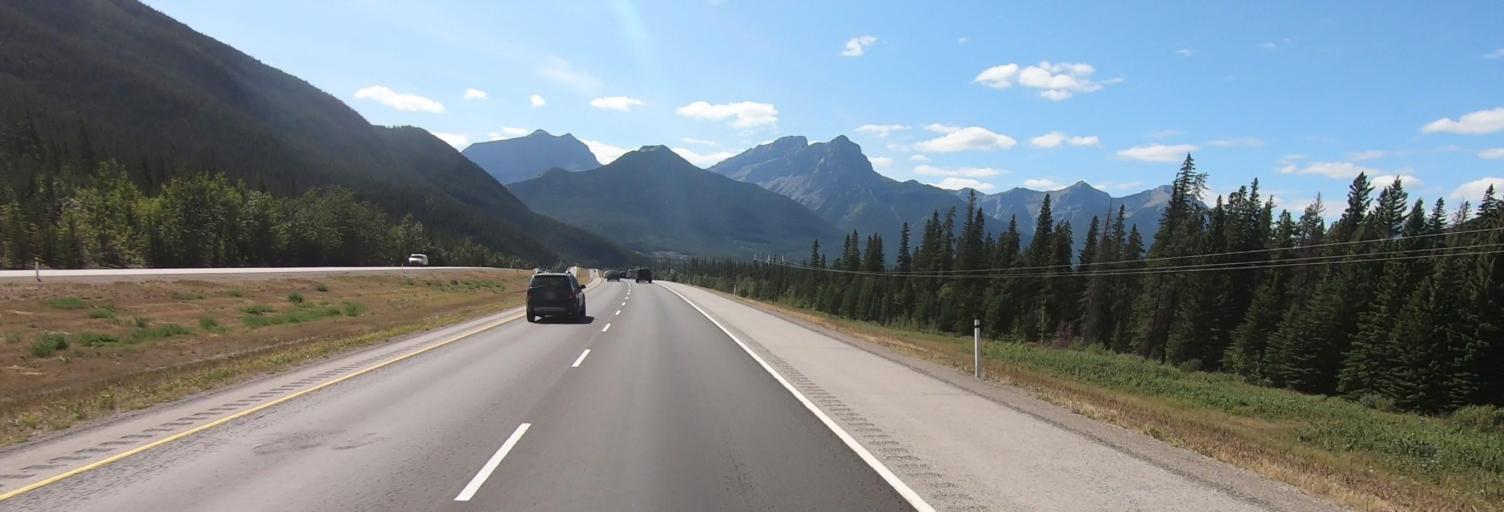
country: CA
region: Alberta
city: Canmore
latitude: 51.0507
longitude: -115.2170
